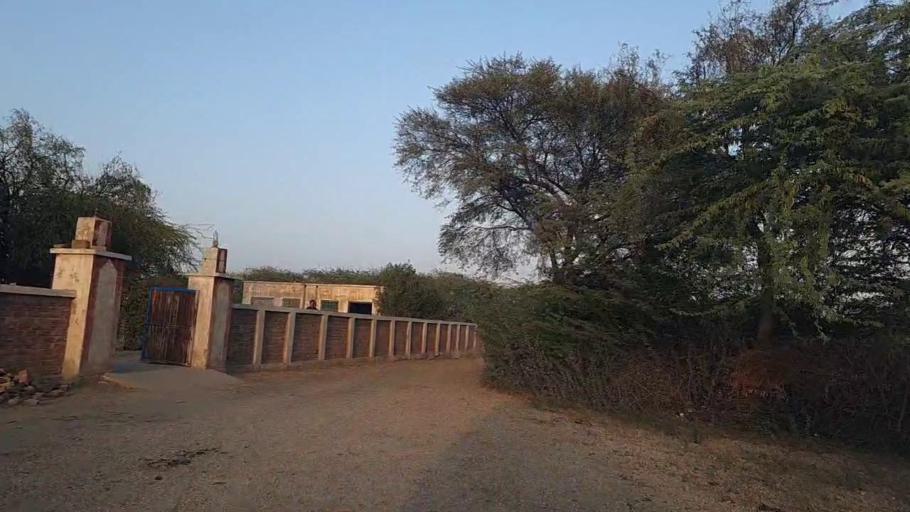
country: PK
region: Sindh
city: Naukot
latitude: 24.7019
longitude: 69.2743
